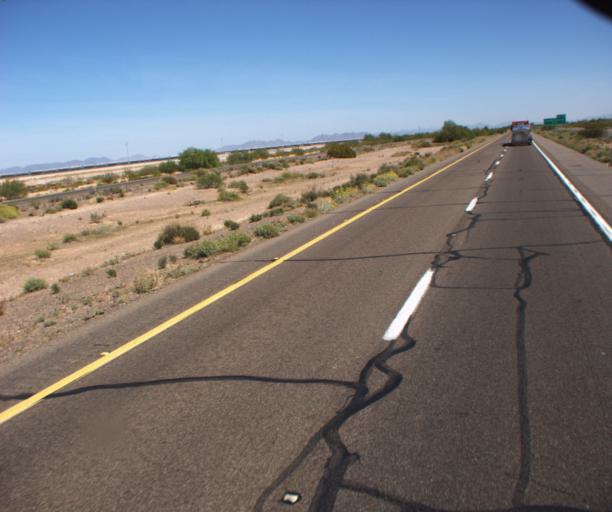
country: US
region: Arizona
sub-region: Maricopa County
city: Gila Bend
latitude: 32.9067
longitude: -112.9826
